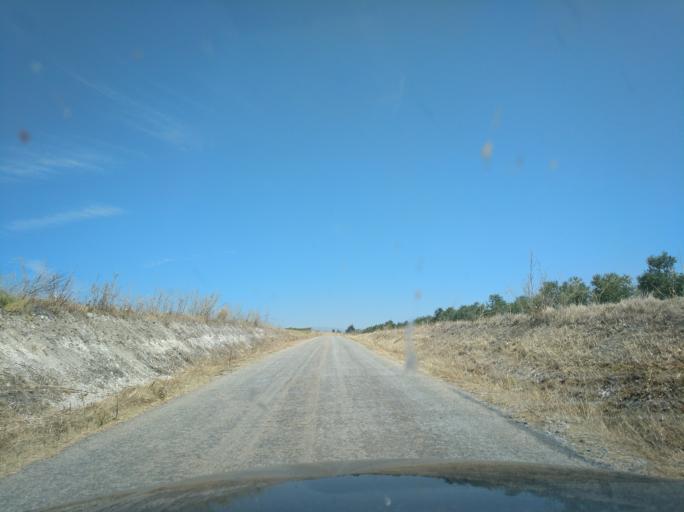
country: PT
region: Portalegre
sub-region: Campo Maior
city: Campo Maior
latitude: 38.9831
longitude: -7.0964
